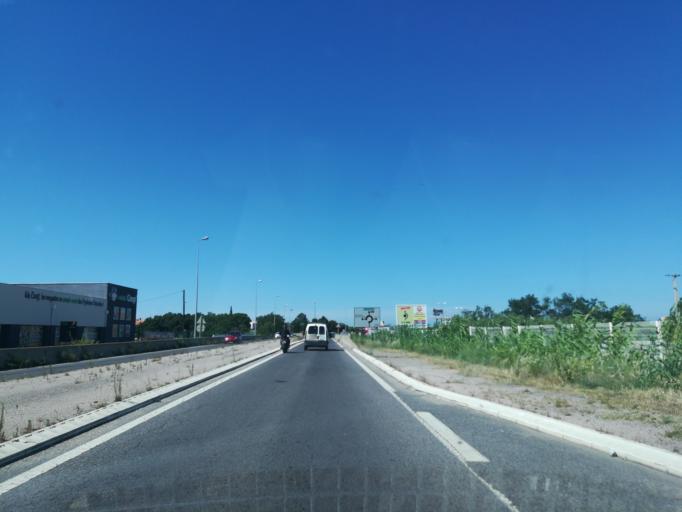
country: FR
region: Languedoc-Roussillon
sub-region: Departement des Pyrenees-Orientales
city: Pollestres
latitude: 42.6391
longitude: 2.8749
